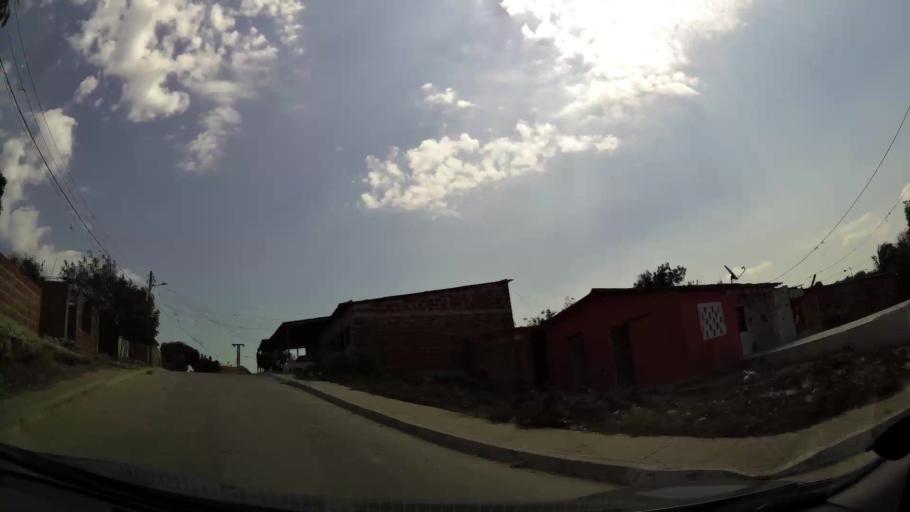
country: CO
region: Atlantico
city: Barranquilla
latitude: 10.9661
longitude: -74.8264
